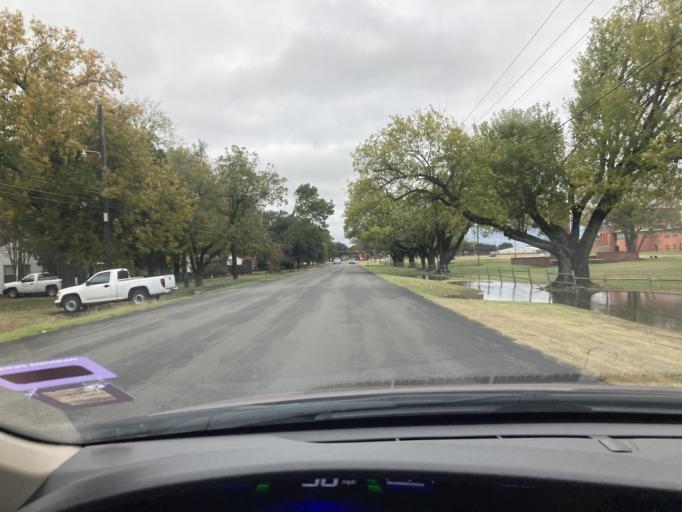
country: US
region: Texas
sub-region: Navarro County
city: Corsicana
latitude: 32.0789
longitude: -96.5050
